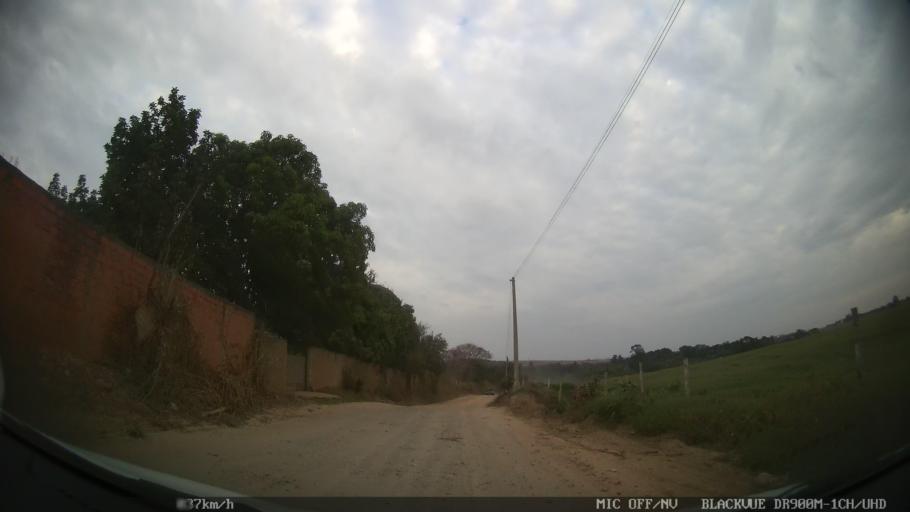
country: BR
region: Sao Paulo
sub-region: Santa Barbara D'Oeste
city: Santa Barbara d'Oeste
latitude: -22.6916
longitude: -47.3873
